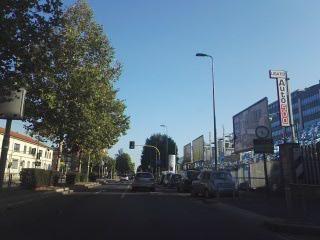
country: IT
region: Lombardy
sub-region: Citta metropolitana di Milano
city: Romano Banco
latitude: 45.4635
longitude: 9.1476
